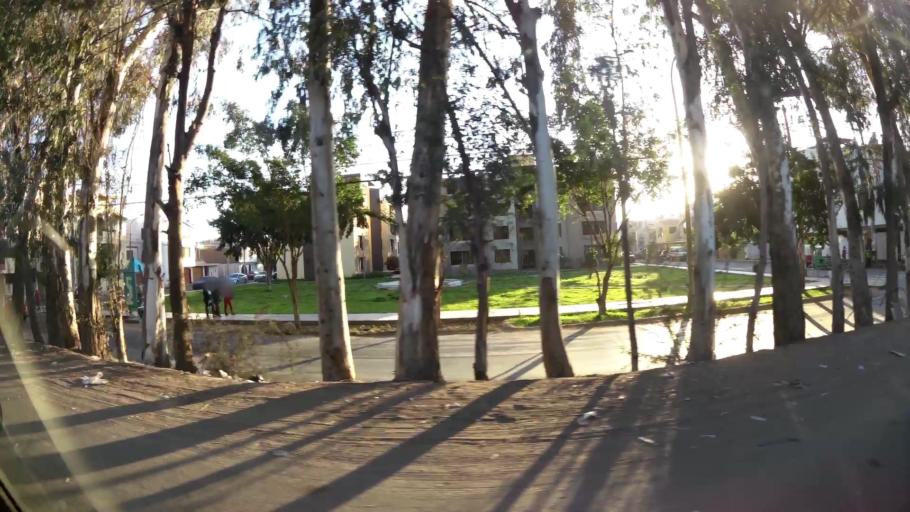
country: PE
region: Ica
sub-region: Provincia de Ica
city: Ica
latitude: -14.0773
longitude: -75.7386
